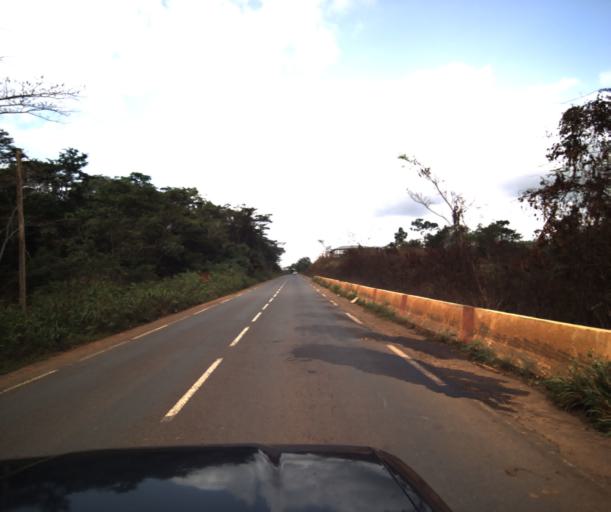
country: CM
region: Centre
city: Mbankomo
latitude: 3.7915
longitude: 11.4149
